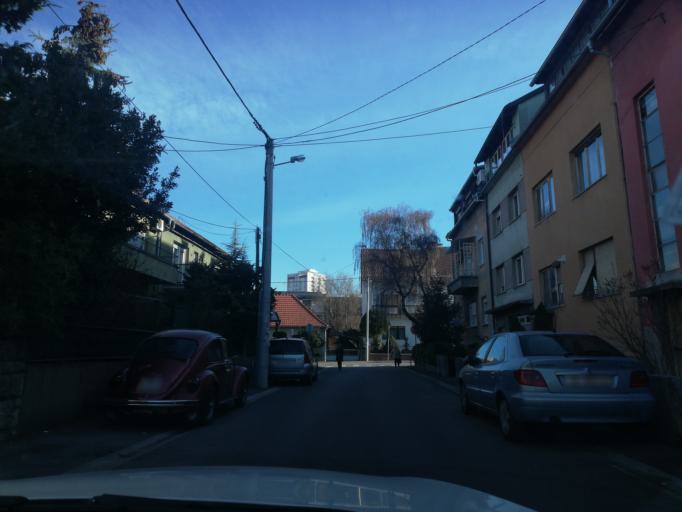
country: HR
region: Grad Zagreb
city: Zagreb - Centar
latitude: 45.7998
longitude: 15.9466
